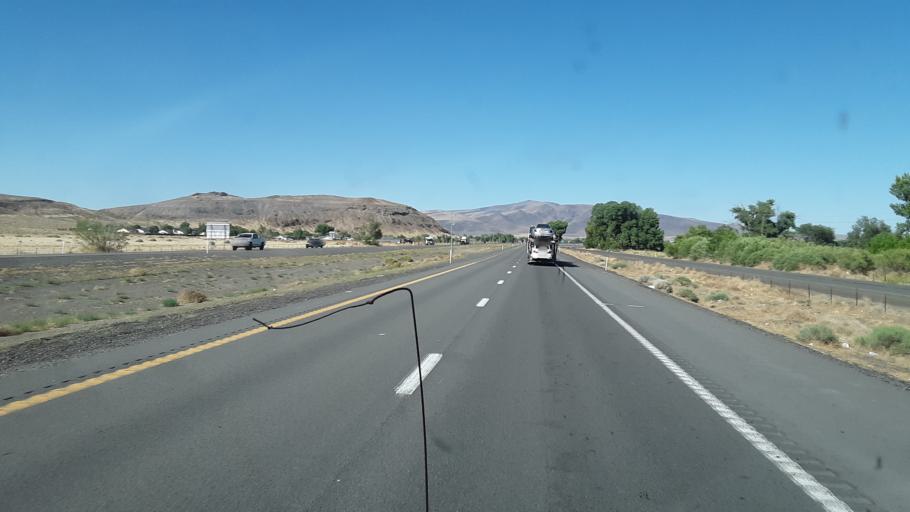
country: US
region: Nevada
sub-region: Lyon County
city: Fernley
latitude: 39.6101
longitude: -119.3177
